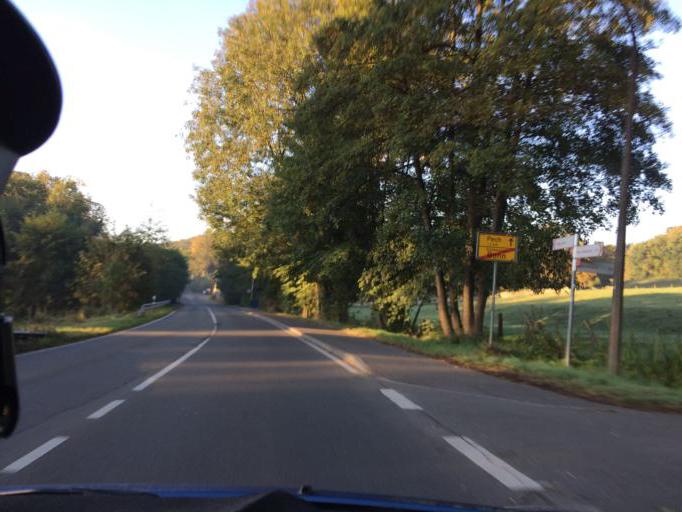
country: DE
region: North Rhine-Westphalia
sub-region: Regierungsbezirk Koln
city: Konigswinter
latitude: 50.6741
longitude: 7.1393
